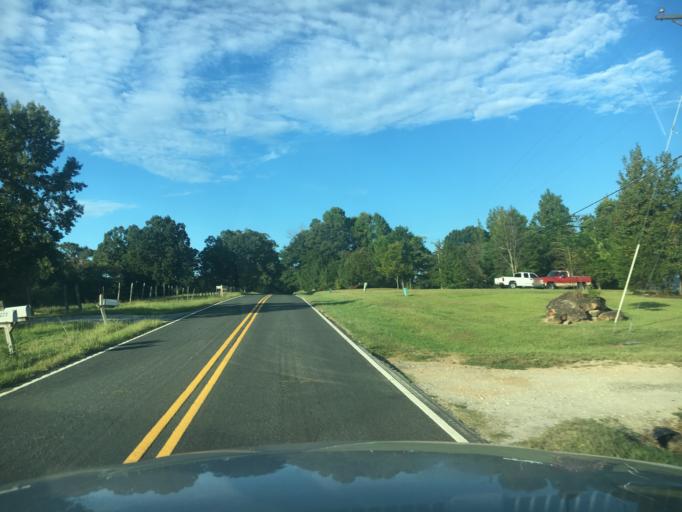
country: US
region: South Carolina
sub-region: Spartanburg County
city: Woodruff
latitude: 34.6299
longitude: -82.0615
